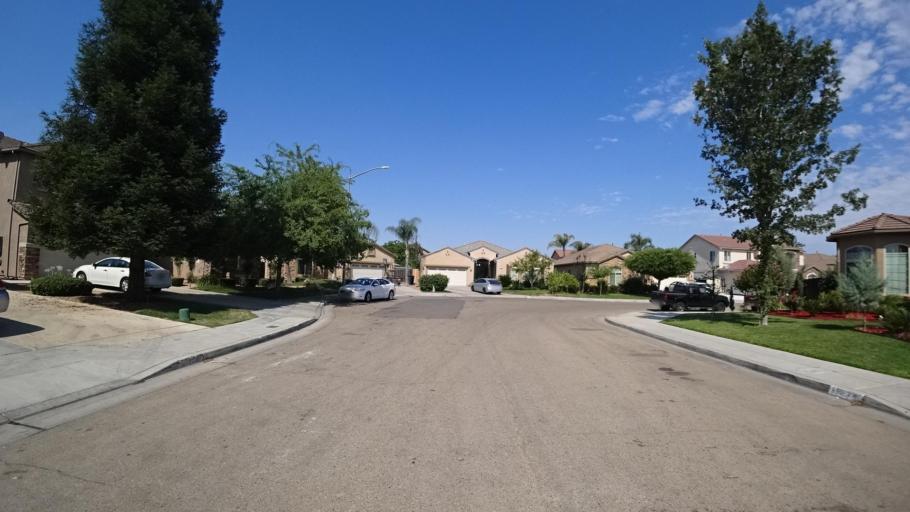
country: US
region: California
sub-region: Fresno County
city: Sunnyside
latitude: 36.7191
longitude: -119.6845
